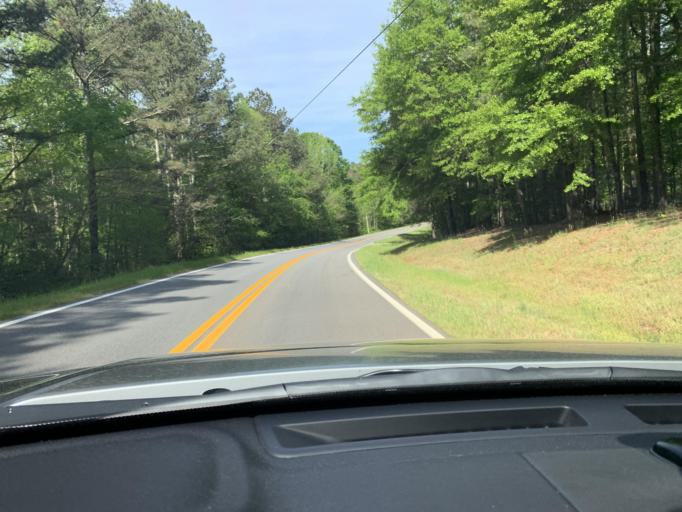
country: US
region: Georgia
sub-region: Oconee County
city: Watkinsville
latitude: 33.8128
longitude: -83.4193
